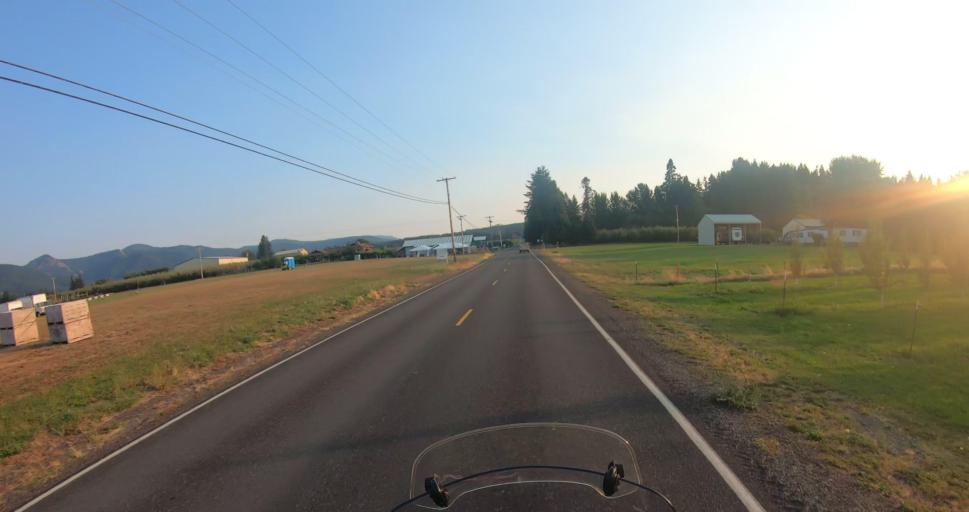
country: US
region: Oregon
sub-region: Hood River County
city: Odell
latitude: 45.4985
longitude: -121.5968
